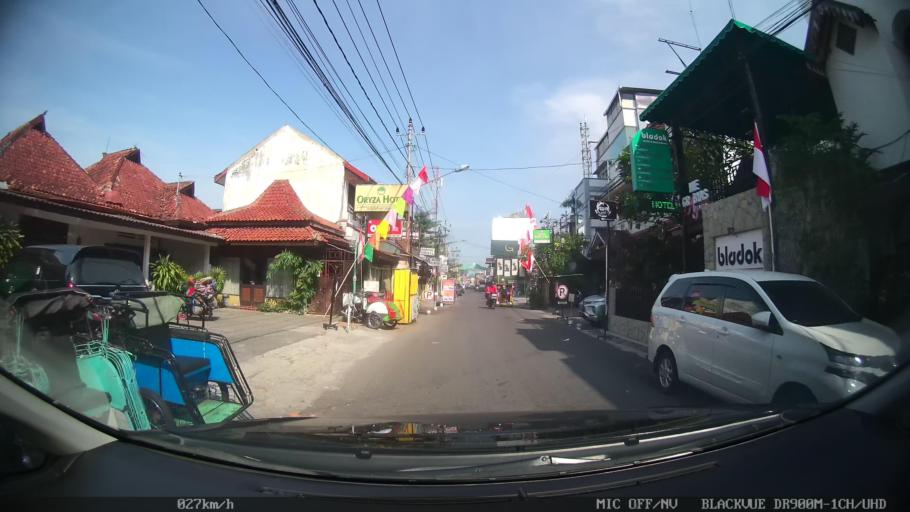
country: ID
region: Daerah Istimewa Yogyakarta
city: Yogyakarta
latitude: -7.7922
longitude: 110.3633
